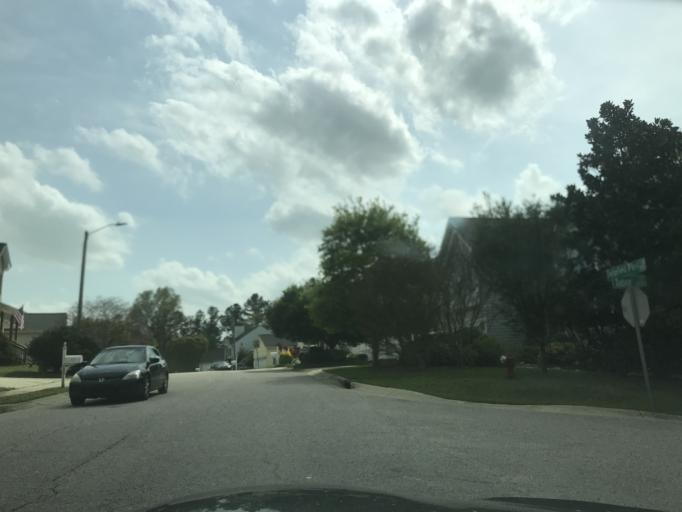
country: US
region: North Carolina
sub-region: Wake County
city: Raleigh
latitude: 35.8198
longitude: -78.5824
